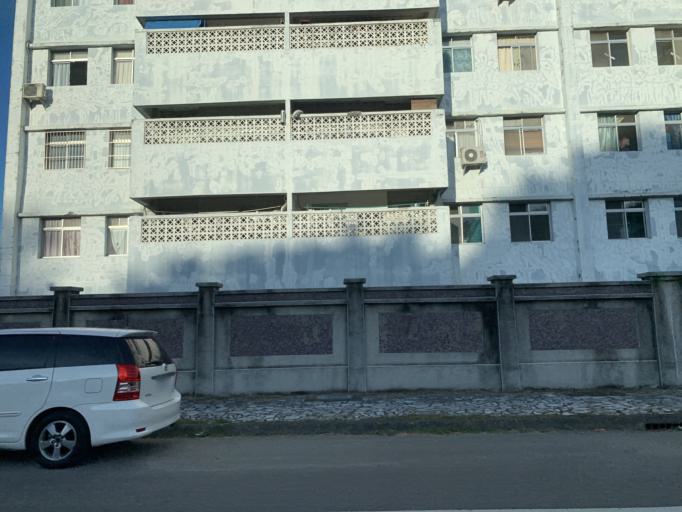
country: TW
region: Taiwan
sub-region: Hualien
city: Hualian
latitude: 24.0015
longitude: 121.6293
